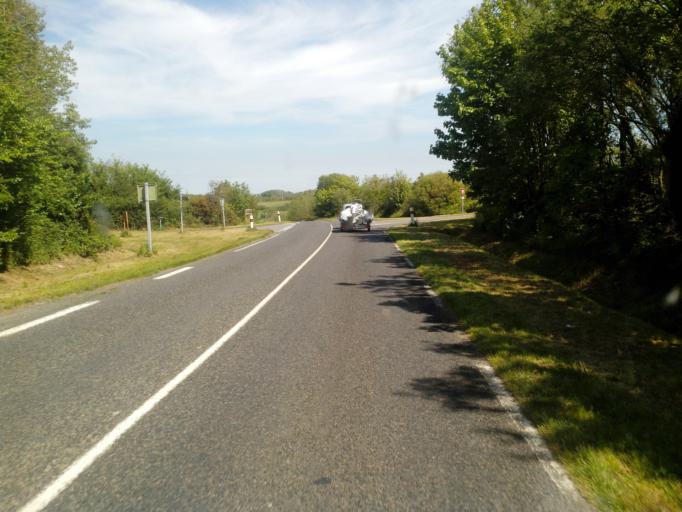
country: FR
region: Nord-Pas-de-Calais
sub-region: Departement du Pas-de-Calais
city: Saint-Martin-Boulogne
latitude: 50.7463
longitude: 1.6192
